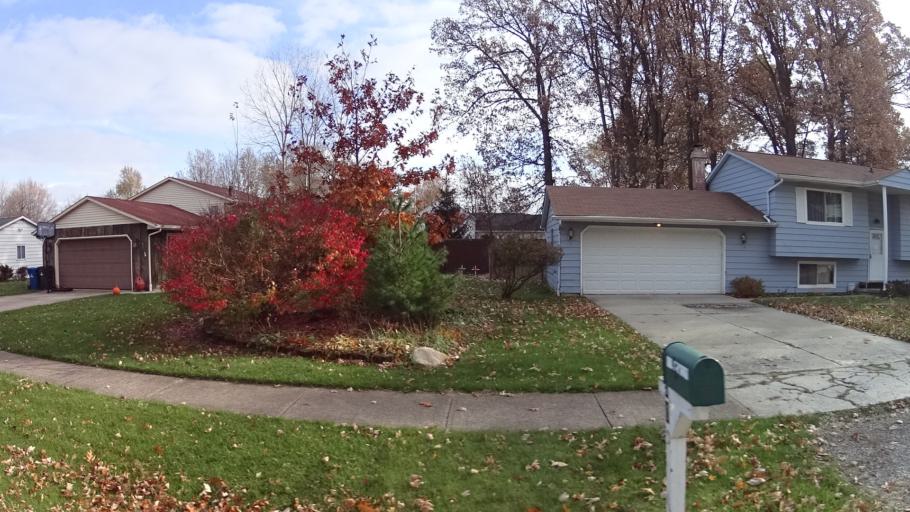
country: US
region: Ohio
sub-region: Lorain County
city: Sheffield Lake
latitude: 41.4810
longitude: -82.1164
